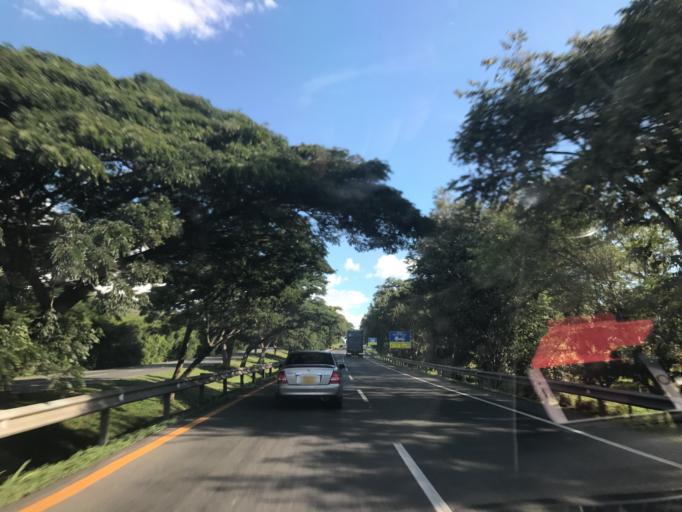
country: CO
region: Valle del Cauca
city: Zarzal
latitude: 4.3084
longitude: -76.0731
